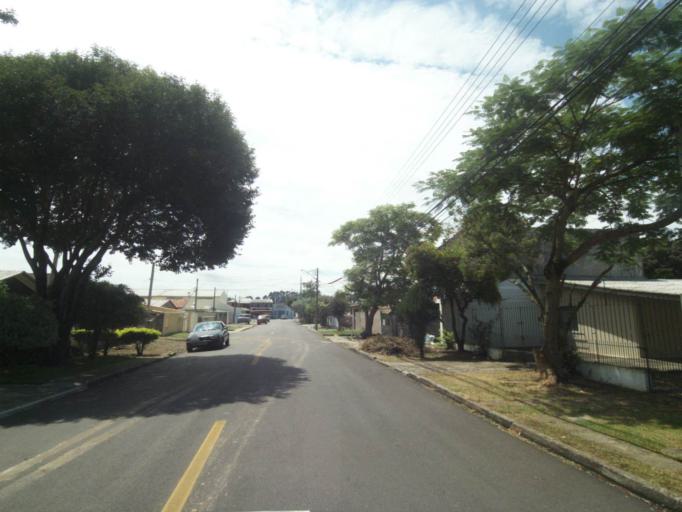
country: BR
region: Parana
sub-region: Pinhais
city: Pinhais
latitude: -25.4725
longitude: -49.1929
